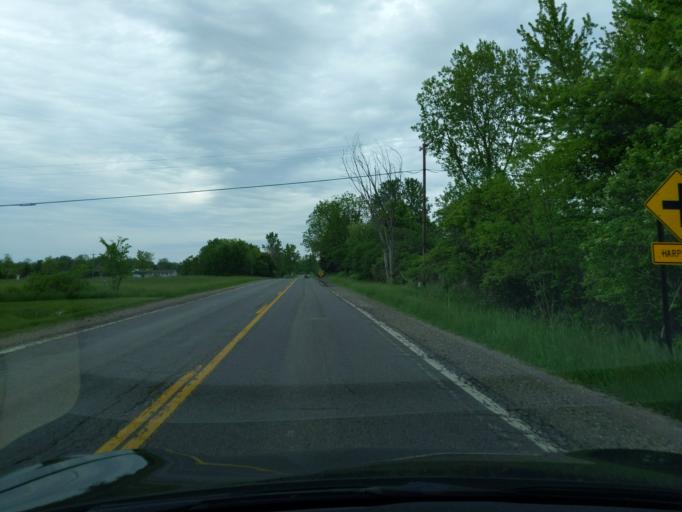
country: US
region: Michigan
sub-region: Ingham County
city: Mason
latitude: 42.6121
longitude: -84.3582
